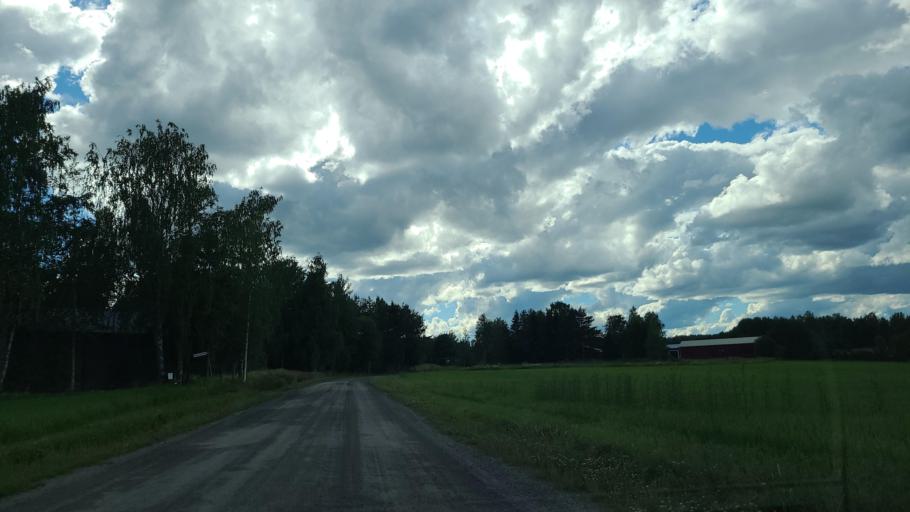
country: FI
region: Central Finland
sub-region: Jaemsae
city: Jaemsae
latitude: 61.9350
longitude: 25.3425
